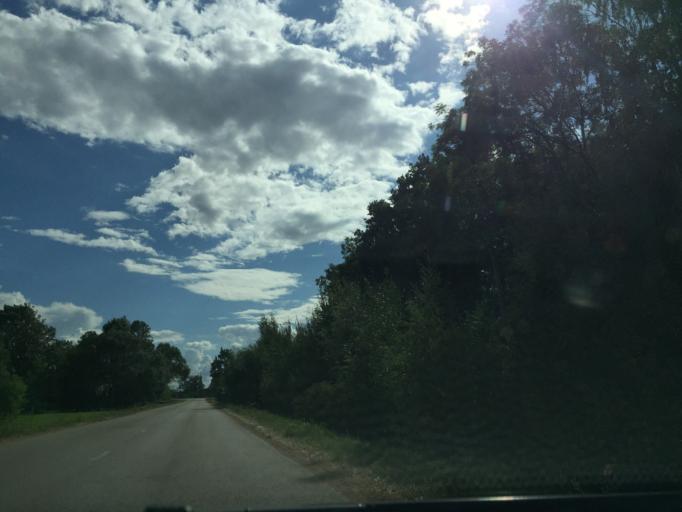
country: LT
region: Siauliu apskritis
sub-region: Joniskis
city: Joniskis
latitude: 56.2478
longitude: 23.5553
